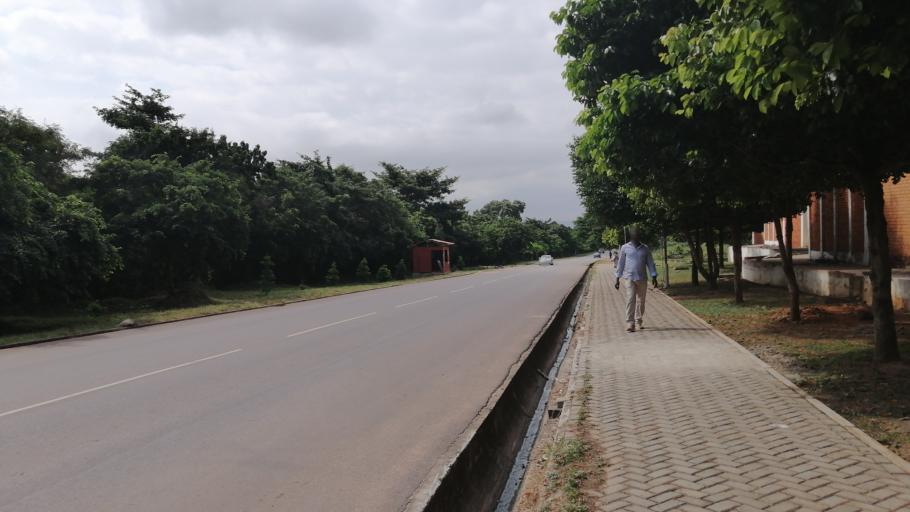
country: GH
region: Greater Accra
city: Medina Estates
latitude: 5.6585
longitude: -0.1825
